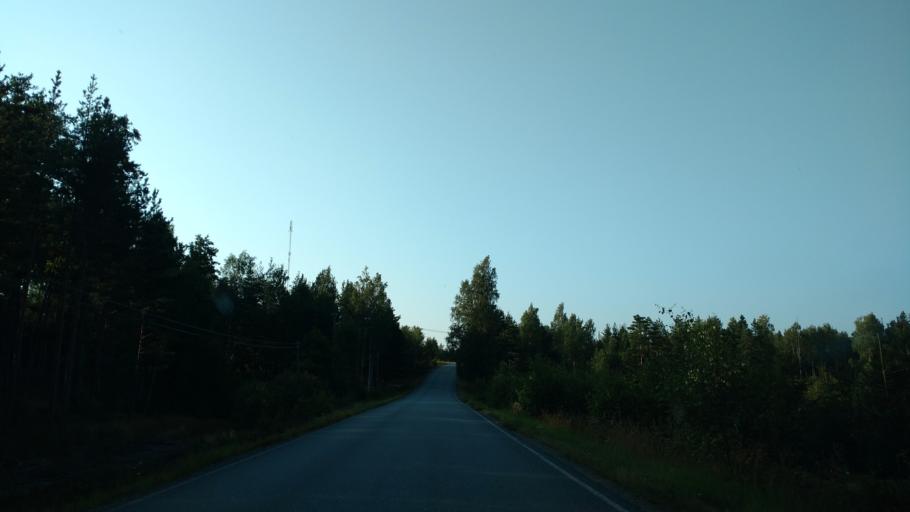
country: FI
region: Varsinais-Suomi
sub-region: Aboland-Turunmaa
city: Dragsfjaerd
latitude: 59.9424
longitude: 22.4148
